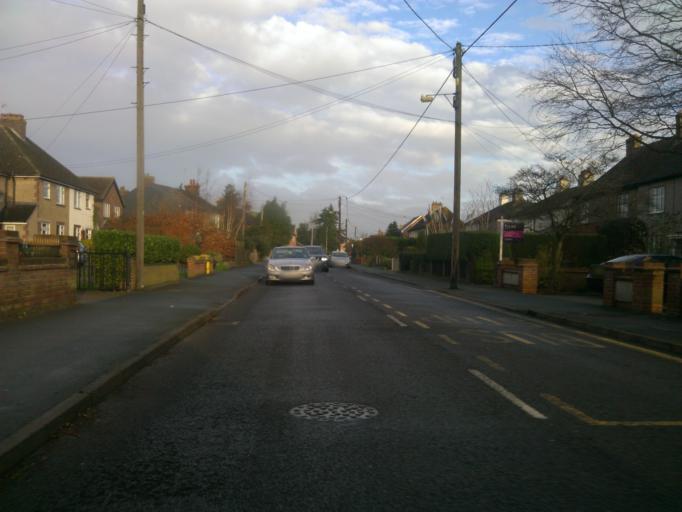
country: GB
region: England
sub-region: Essex
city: Wivenhoe
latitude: 51.8643
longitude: 0.9637
